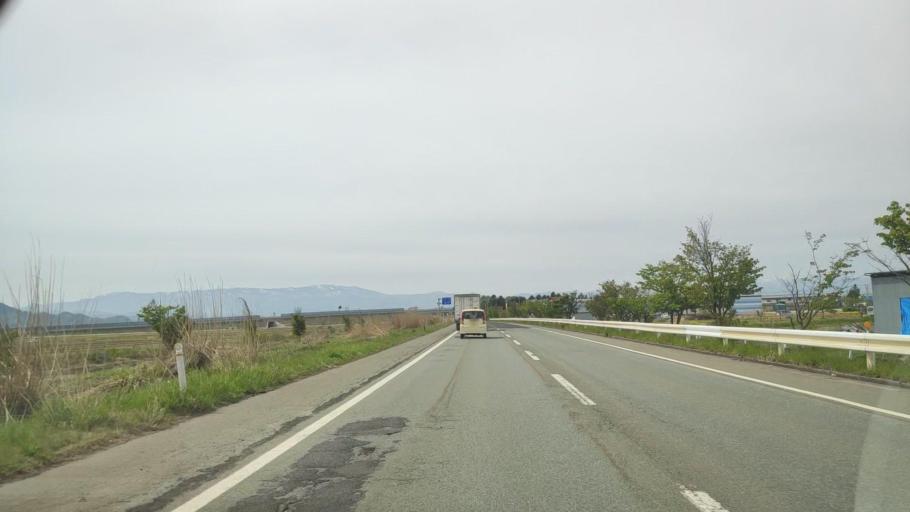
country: JP
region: Yamagata
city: Takahata
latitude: 38.0340
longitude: 140.1722
